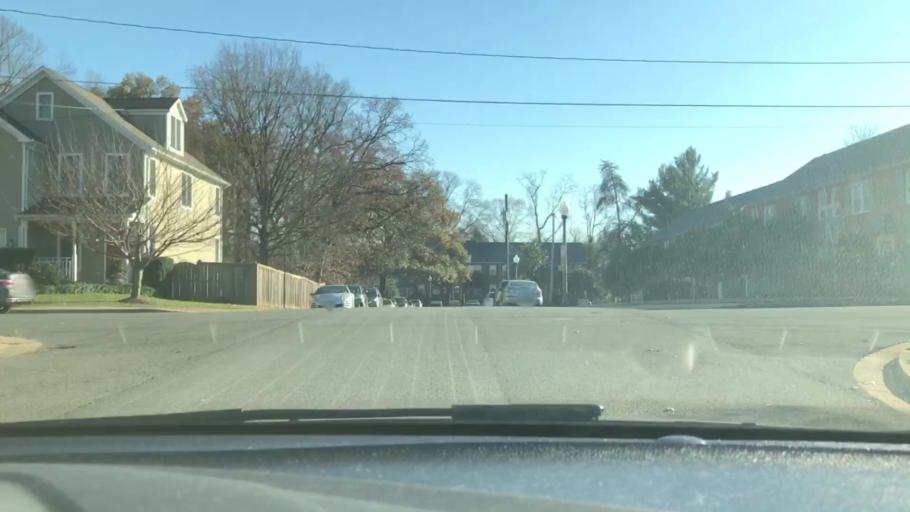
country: US
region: Virginia
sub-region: Arlington County
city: Arlington
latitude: 38.8804
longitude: -77.1019
